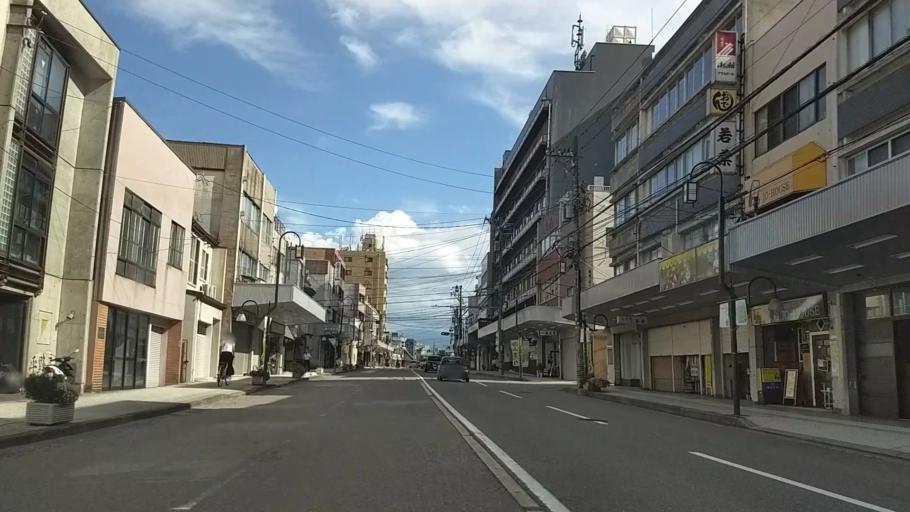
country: JP
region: Ishikawa
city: Nonoichi
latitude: 36.5544
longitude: 136.6717
